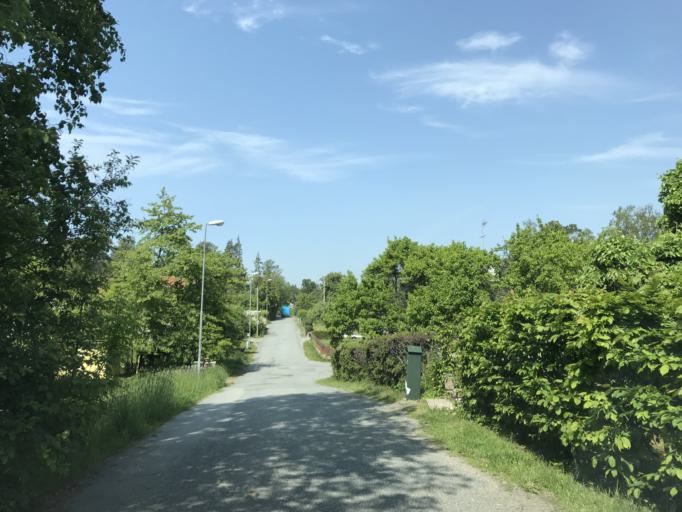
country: SE
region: Stockholm
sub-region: Stockholms Kommun
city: Kista
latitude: 59.4181
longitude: 17.9344
